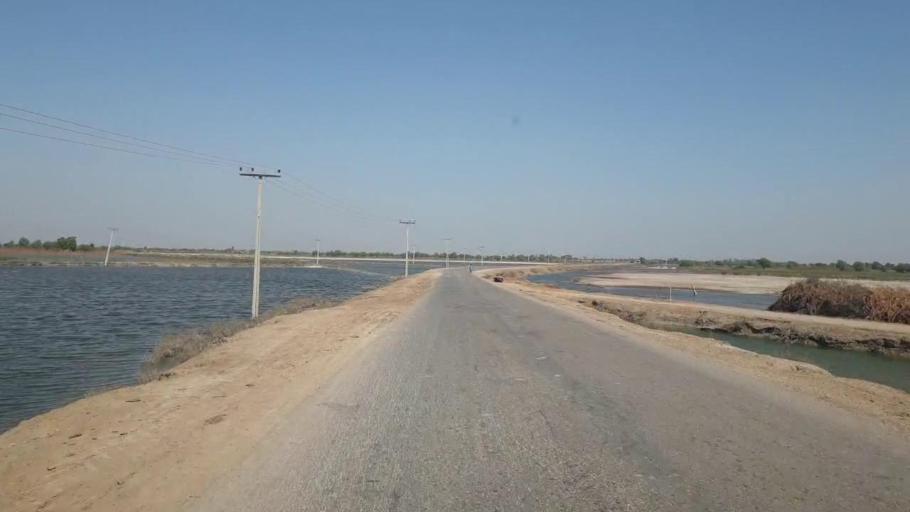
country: PK
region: Sindh
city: Talhar
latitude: 24.9057
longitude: 68.8383
